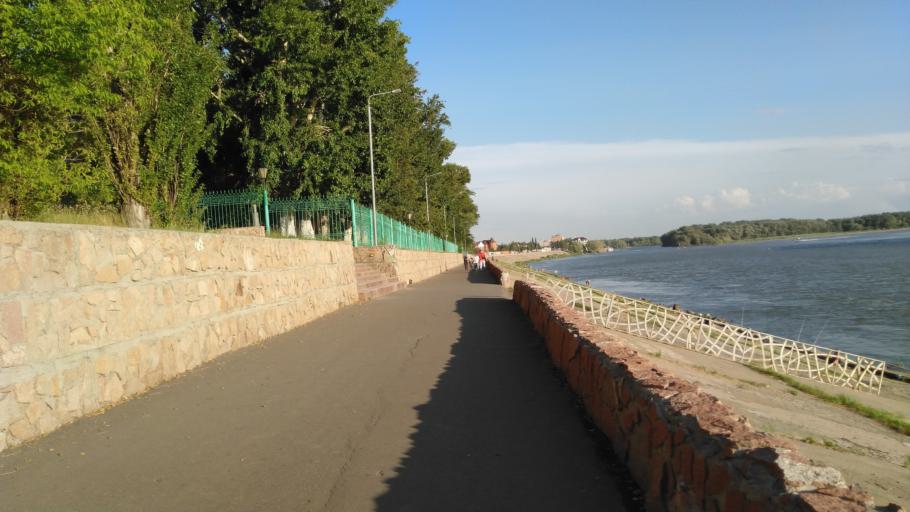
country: KZ
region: Pavlodar
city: Pavlodar
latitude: 52.2766
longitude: 76.9335
